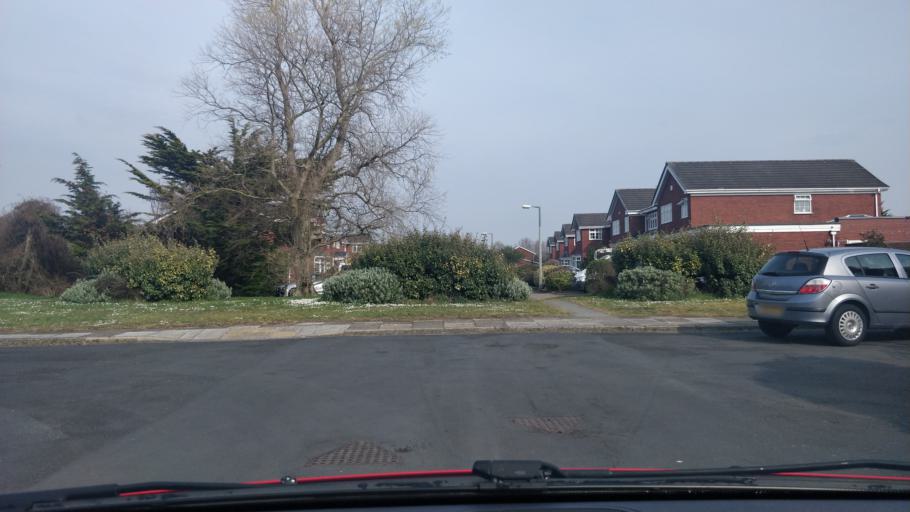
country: GB
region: England
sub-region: Sefton
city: Formby
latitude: 53.6001
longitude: -3.0520
